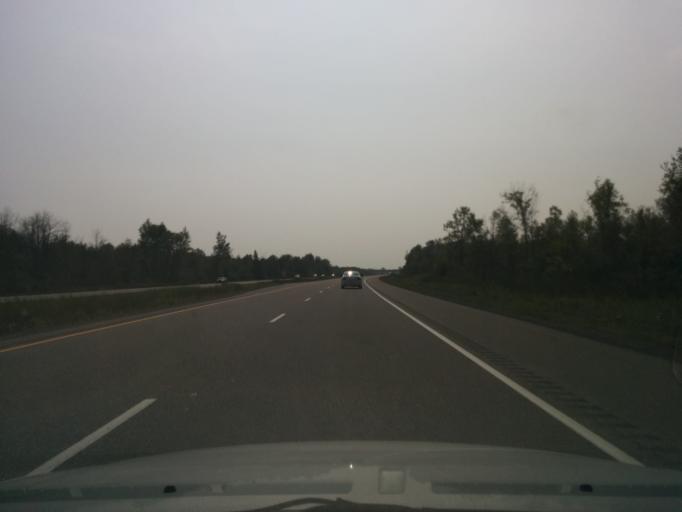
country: CA
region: Ontario
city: Bells Corners
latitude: 45.1028
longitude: -75.6594
